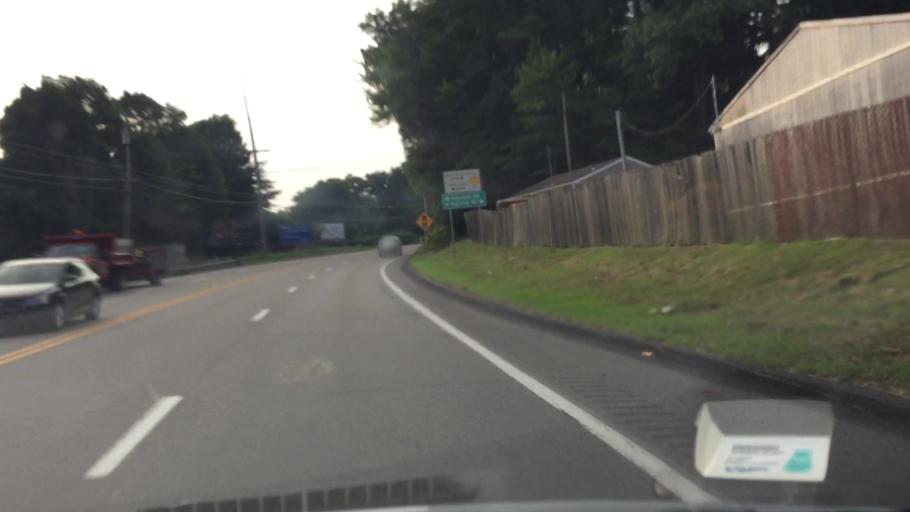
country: US
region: Pennsylvania
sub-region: Allegheny County
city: Franklin Park
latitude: 40.5838
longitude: -80.0405
